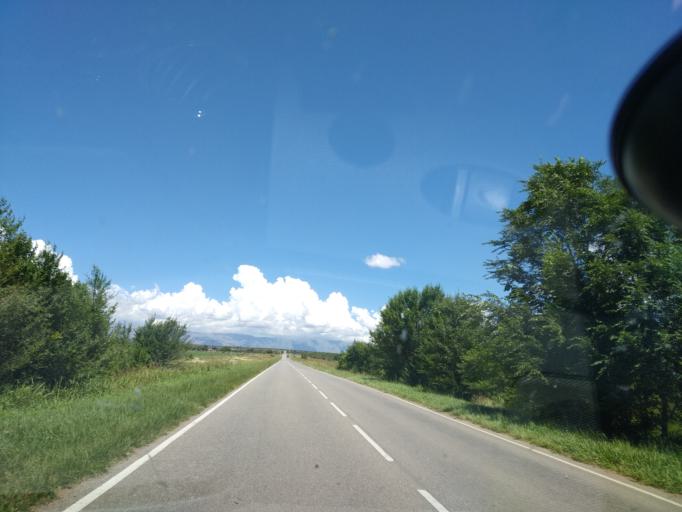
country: AR
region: Cordoba
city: Villa Cura Brochero
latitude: -31.6726
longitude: -65.0922
